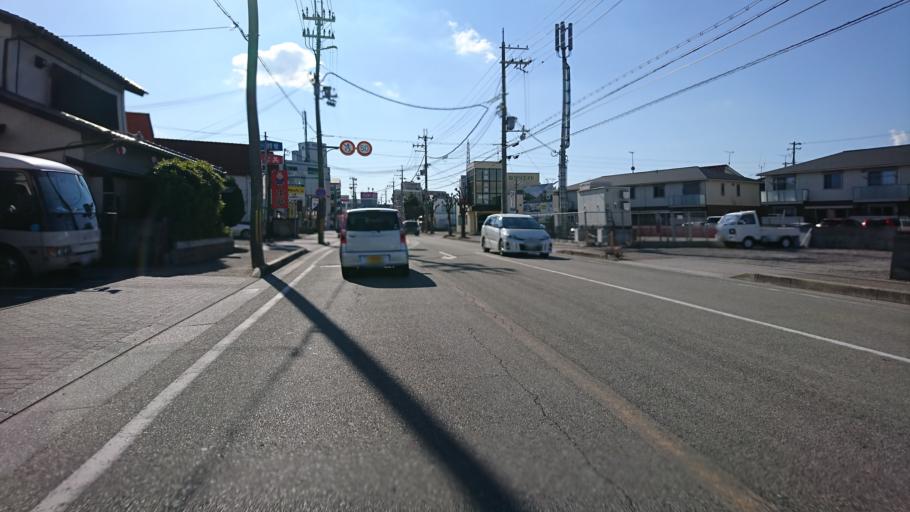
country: JP
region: Hyogo
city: Kakogawacho-honmachi
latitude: 34.7739
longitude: 134.8034
